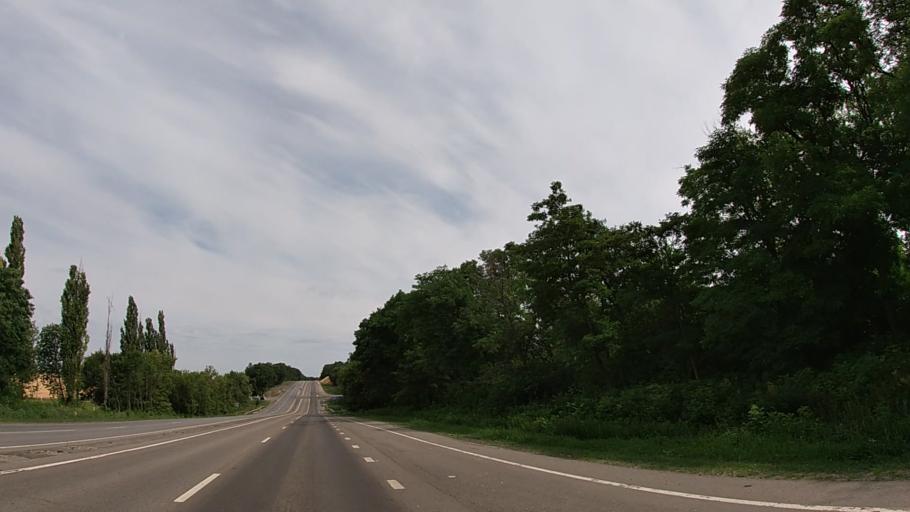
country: RU
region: Belgorod
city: Mayskiy
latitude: 50.4712
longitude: 36.4047
